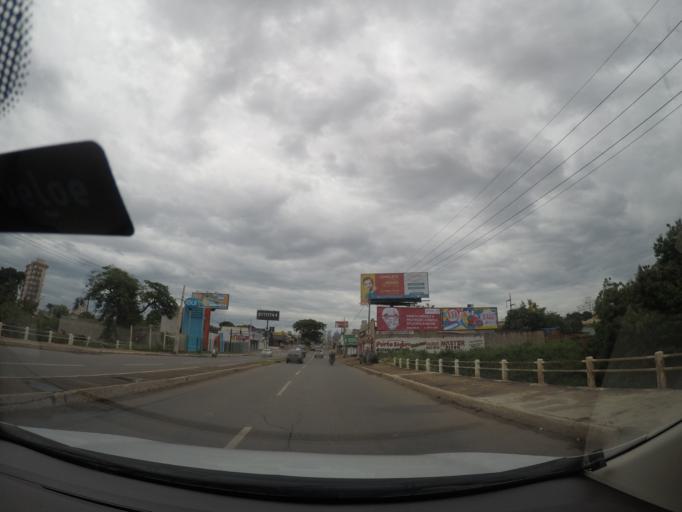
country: BR
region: Goias
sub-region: Goiania
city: Goiania
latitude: -16.7103
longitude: -49.2958
